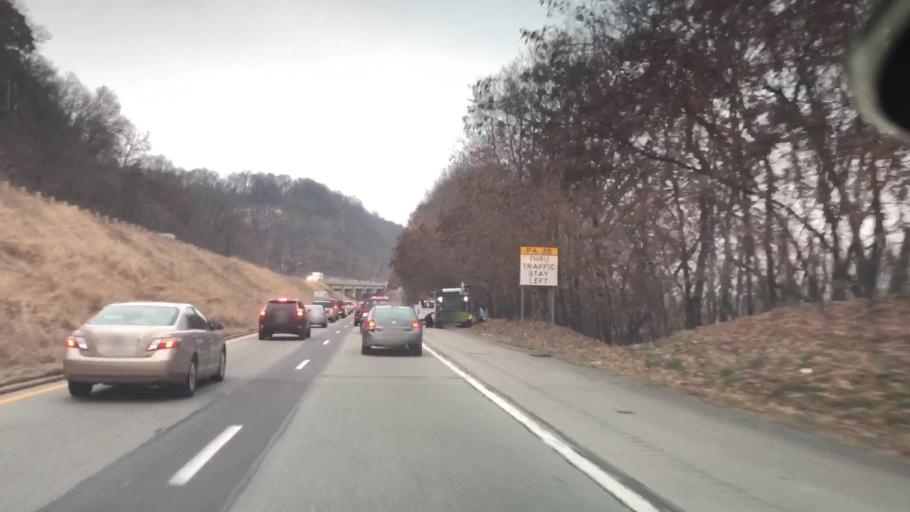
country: US
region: Pennsylvania
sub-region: Allegheny County
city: Sharpsburg
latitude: 40.4973
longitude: -79.9290
